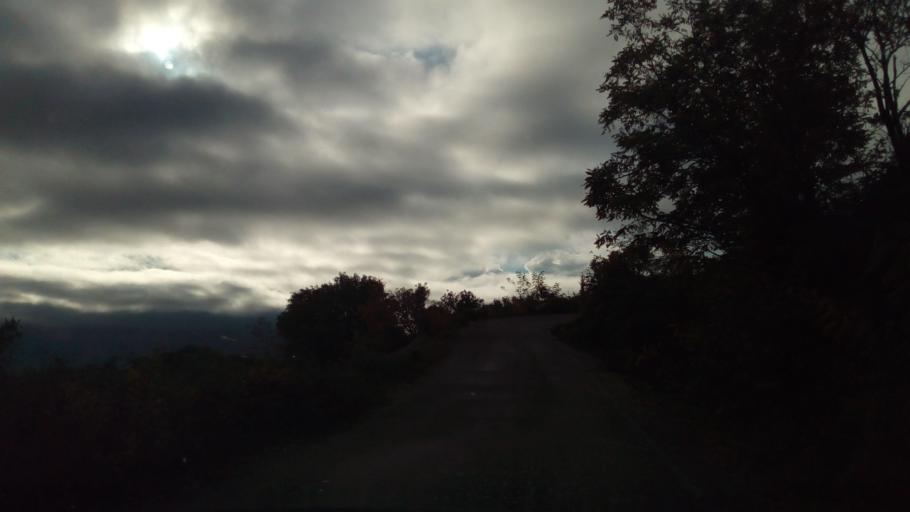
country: GR
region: West Greece
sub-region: Nomos Aitolias kai Akarnanias
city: Nafpaktos
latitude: 38.5222
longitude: 21.9785
